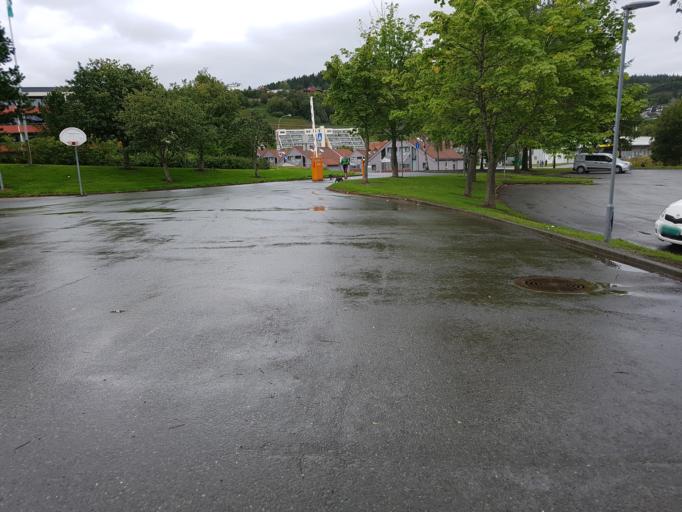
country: NO
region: Sor-Trondelag
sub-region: Trondheim
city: Trondheim
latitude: 63.4000
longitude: 10.4335
